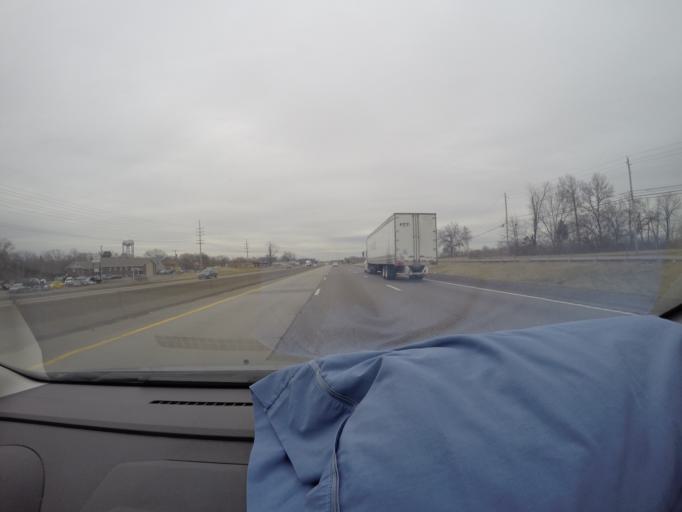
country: US
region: Missouri
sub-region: Saint Charles County
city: O'Fallon
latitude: 38.8027
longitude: -90.7207
